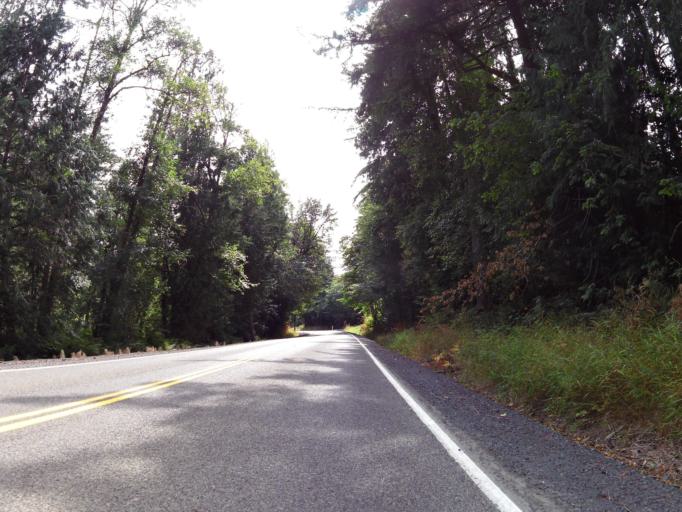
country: US
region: Washington
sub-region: Lewis County
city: Napavine
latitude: 46.5479
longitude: -122.9549
